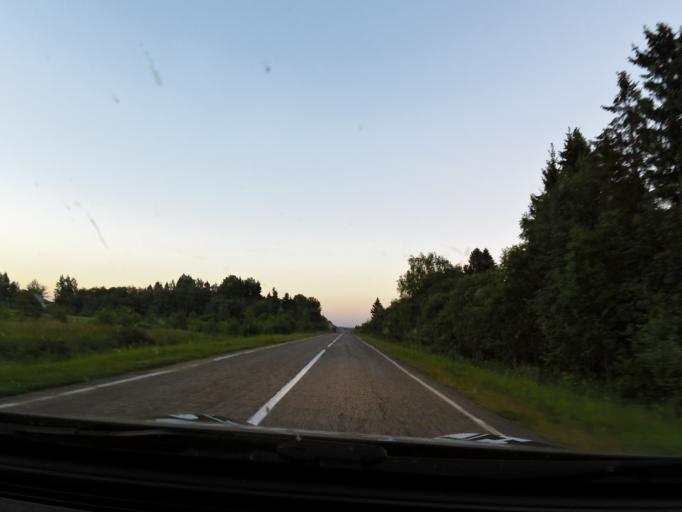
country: RU
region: Kostroma
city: Buy
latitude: 58.3483
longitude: 41.1513
